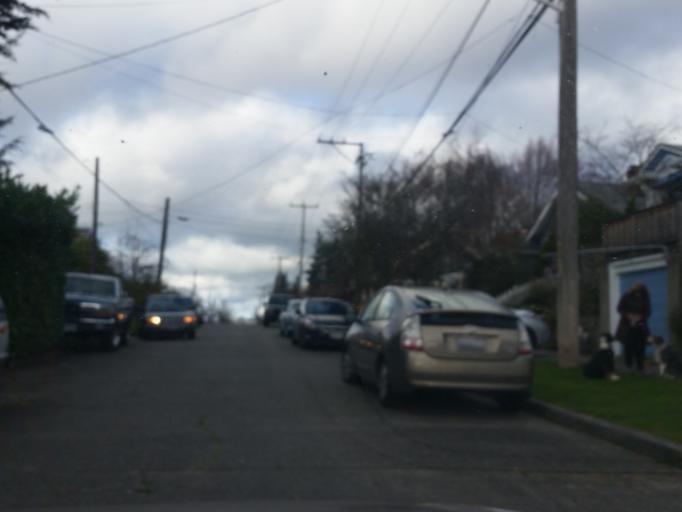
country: US
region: Washington
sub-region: King County
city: Seattle
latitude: 47.6713
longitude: -122.3554
